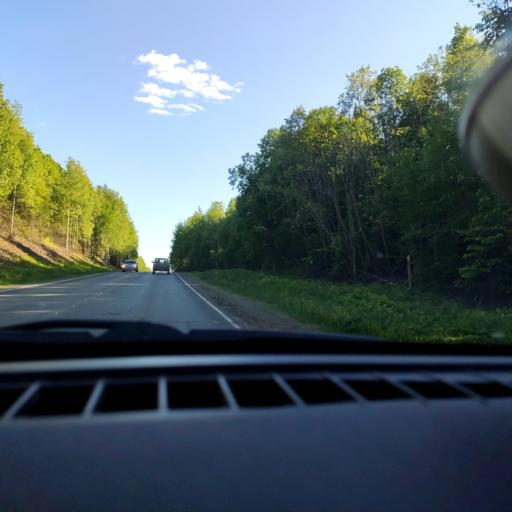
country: RU
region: Perm
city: Polazna
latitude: 58.2586
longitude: 56.1653
